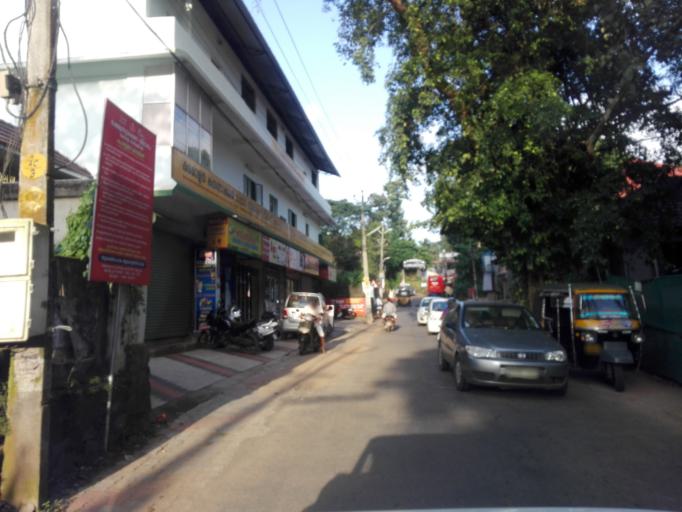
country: IN
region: Kerala
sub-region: Kottayam
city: Kottayam
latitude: 9.6123
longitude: 76.4981
